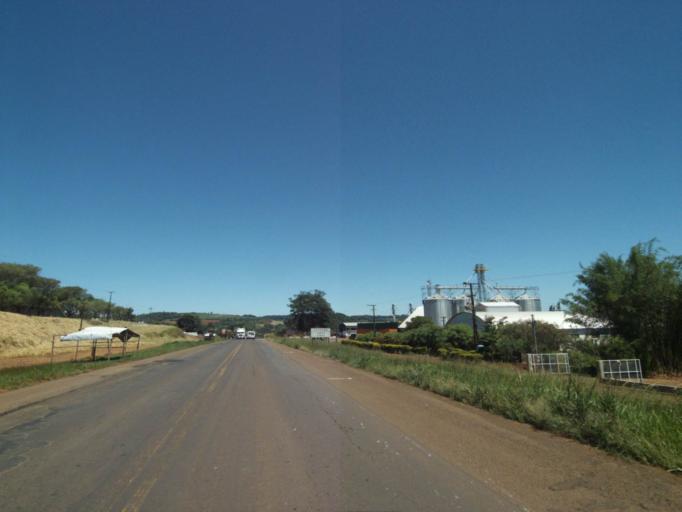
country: BR
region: Parana
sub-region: Pato Branco
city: Pato Branco
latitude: -26.2596
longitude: -52.7705
